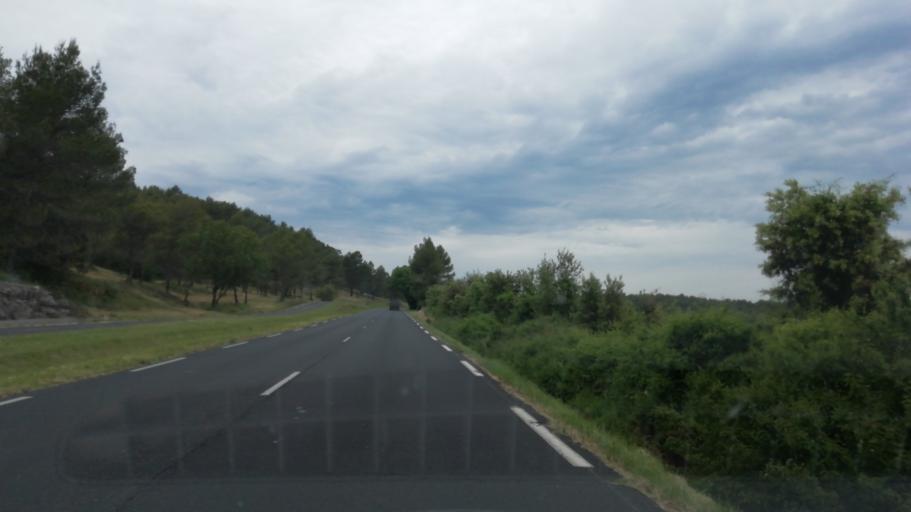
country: FR
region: Languedoc-Roussillon
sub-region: Departement de l'Herault
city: Prades-le-Lez
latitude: 43.7033
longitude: 3.8504
